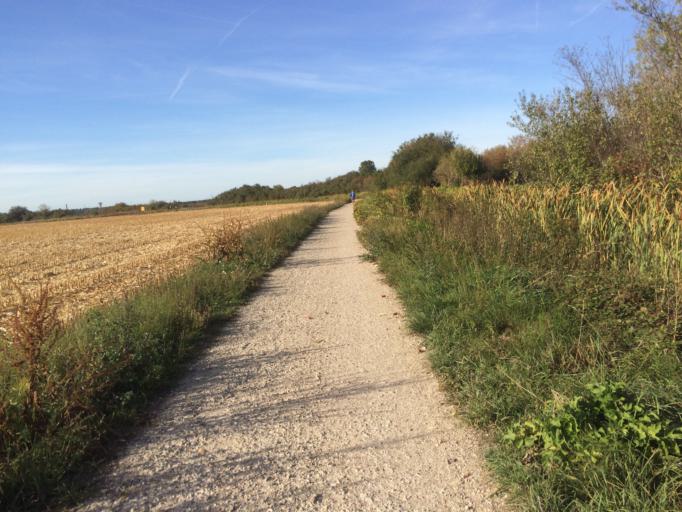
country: FR
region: Ile-de-France
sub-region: Departement de l'Essonne
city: Vauhallan
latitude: 48.7250
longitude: 2.1996
